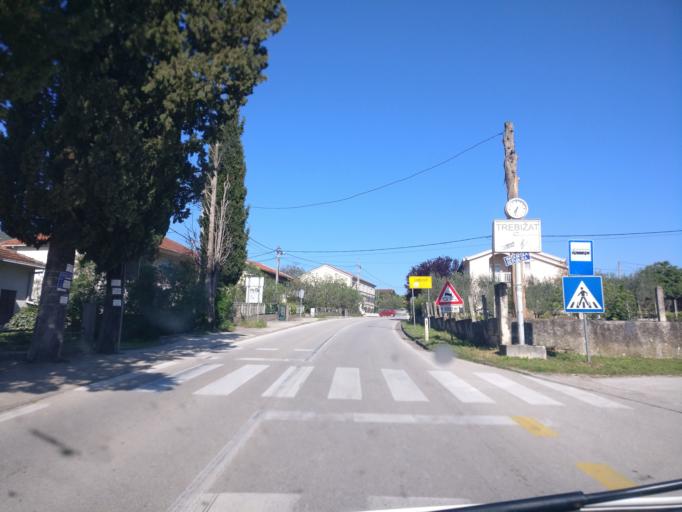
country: BA
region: Federation of Bosnia and Herzegovina
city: Capljina
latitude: 43.1216
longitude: 17.6852
